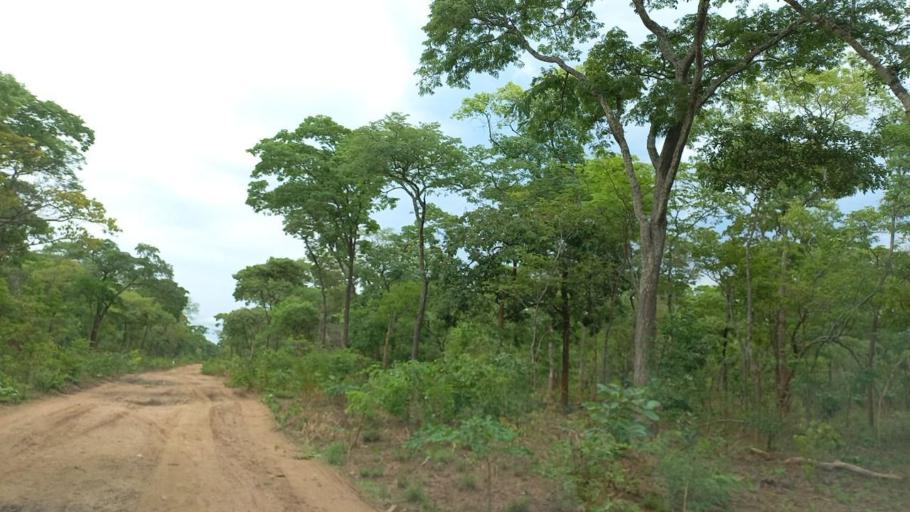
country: ZM
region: North-Western
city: Kalengwa
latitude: -13.5465
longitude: 24.9764
